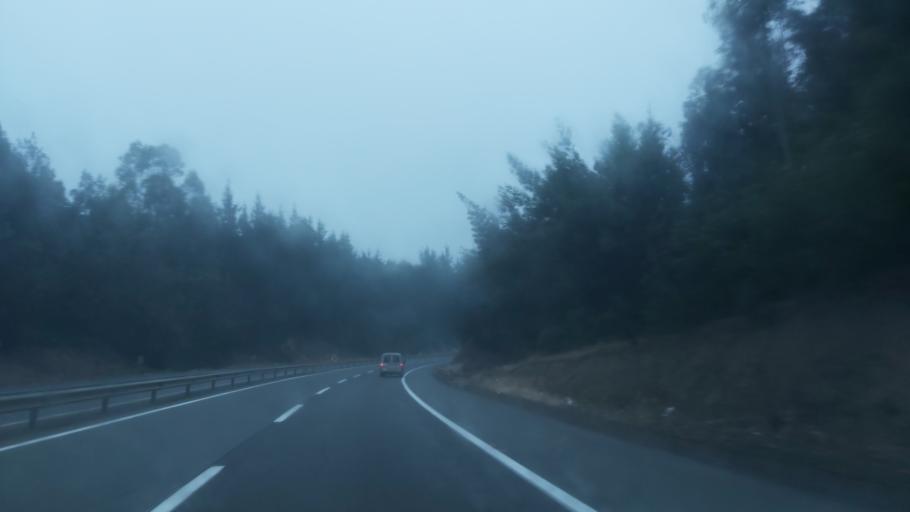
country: CL
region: Biobio
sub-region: Provincia de Concepcion
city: Penco
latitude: -36.7405
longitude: -72.9026
